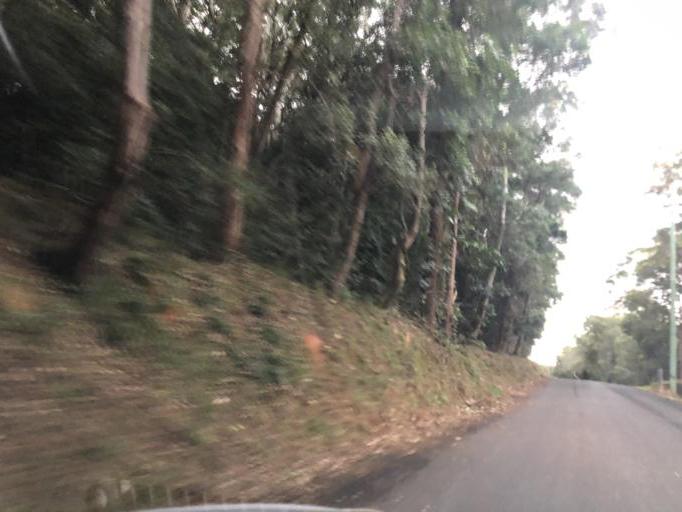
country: AU
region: New South Wales
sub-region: Coffs Harbour
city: Coffs Harbour
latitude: -30.3095
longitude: 153.1301
